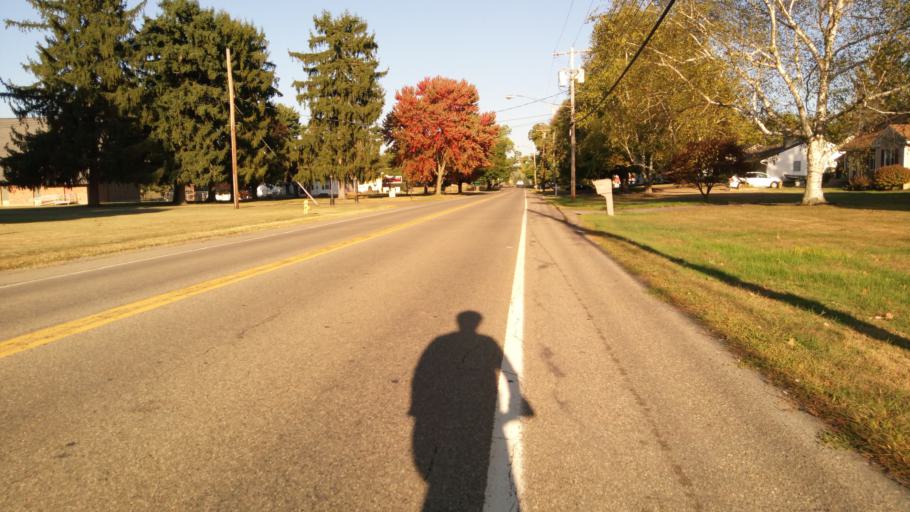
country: US
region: New York
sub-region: Chemung County
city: Southport
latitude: 42.0534
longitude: -76.8263
